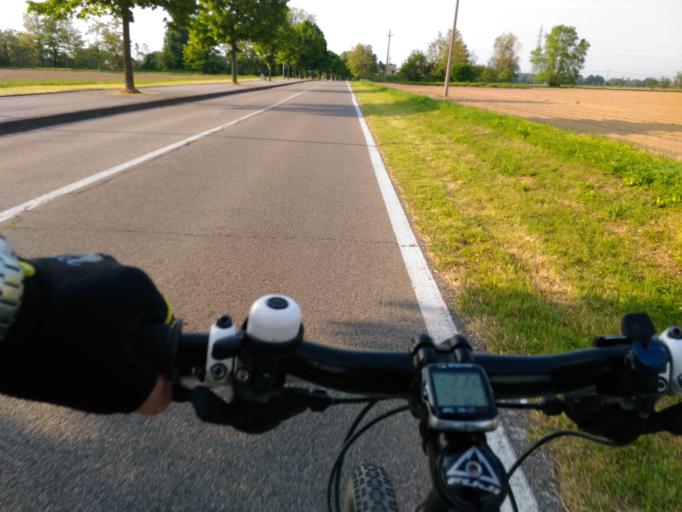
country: IT
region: Lombardy
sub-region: Citta metropolitana di Milano
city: Vizzolo Predabissi
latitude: 45.3631
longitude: 9.3463
